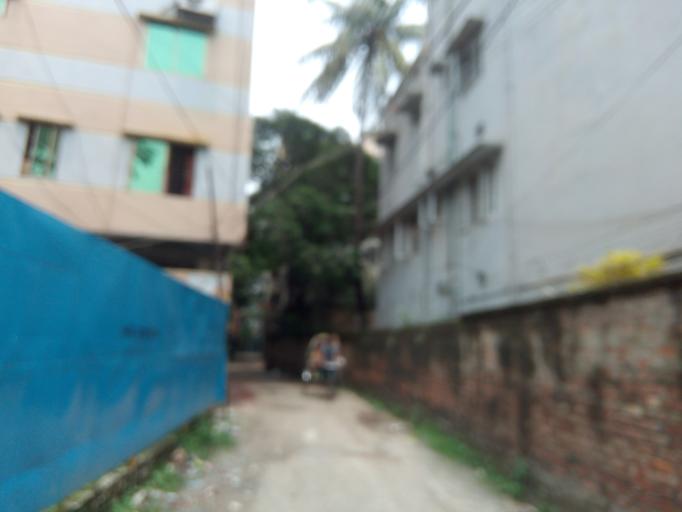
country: BD
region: Dhaka
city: Azimpur
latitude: 23.7442
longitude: 90.3690
